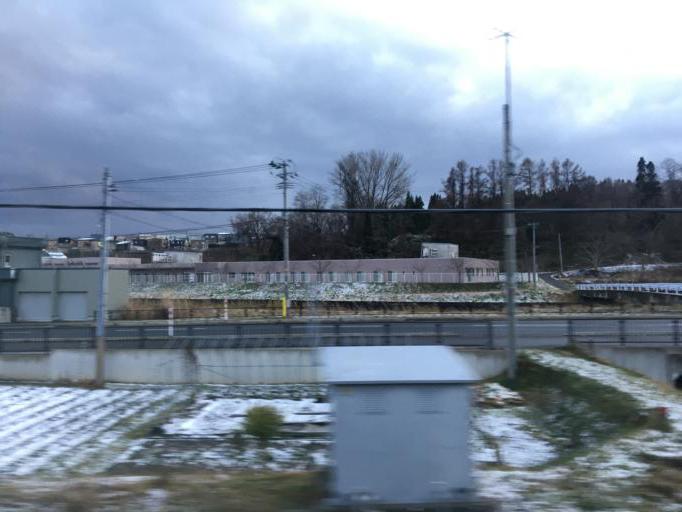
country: JP
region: Aomori
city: Aomori Shi
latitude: 40.8267
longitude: 140.6675
